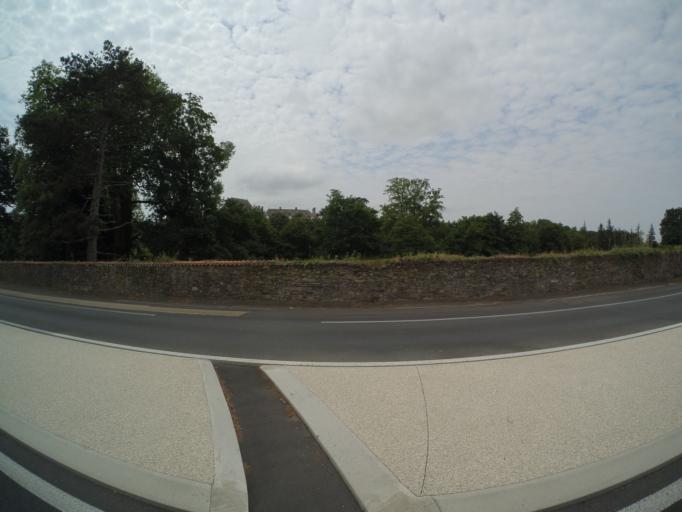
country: FR
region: Pays de la Loire
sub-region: Departement de la Vendee
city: Chavagnes-en-Paillers
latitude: 46.9023
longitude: -1.2318
